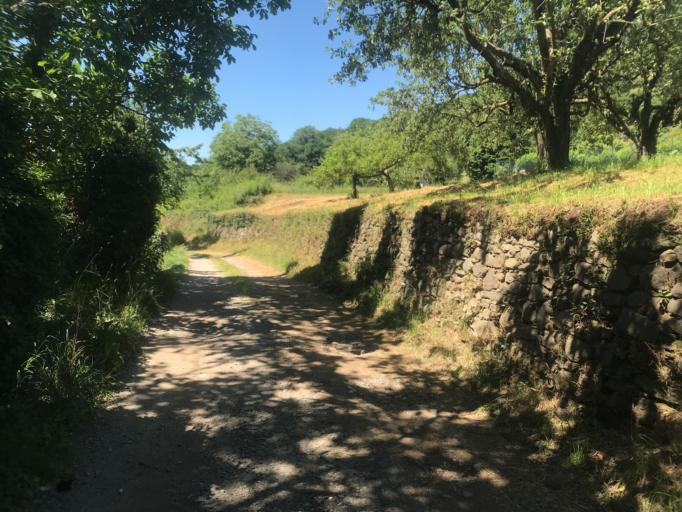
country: IT
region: Piedmont
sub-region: Provincia di Novara
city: Pisano
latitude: 45.7995
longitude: 8.5133
